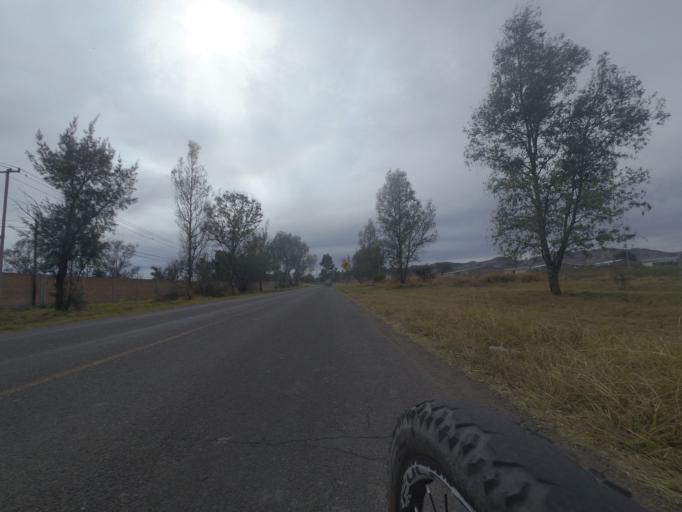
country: MX
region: Aguascalientes
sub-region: Aguascalientes
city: La Loma de los Negritos
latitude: 21.8375
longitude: -102.3562
